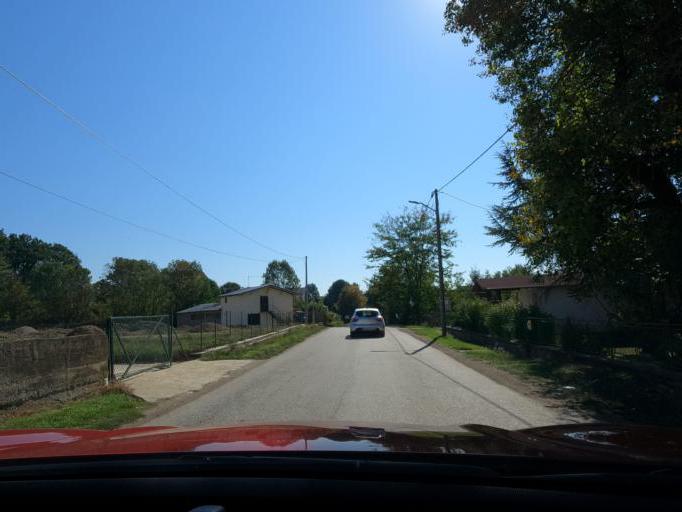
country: RS
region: Central Serbia
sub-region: Raski Okrug
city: Kraljevo
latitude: 43.7652
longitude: 20.6722
